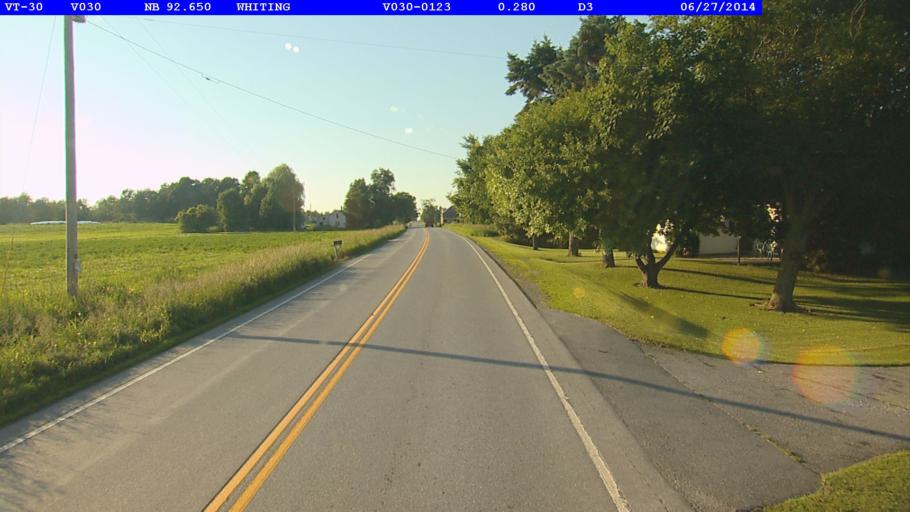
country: US
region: Vermont
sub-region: Rutland County
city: Brandon
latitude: 43.8423
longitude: -73.1954
